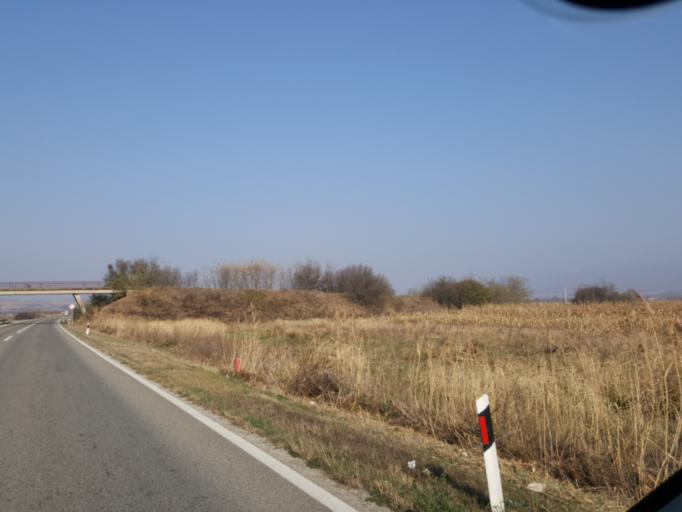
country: RS
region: Central Serbia
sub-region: Jablanicki Okrug
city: Leskovac
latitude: 43.0324
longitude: 21.9419
